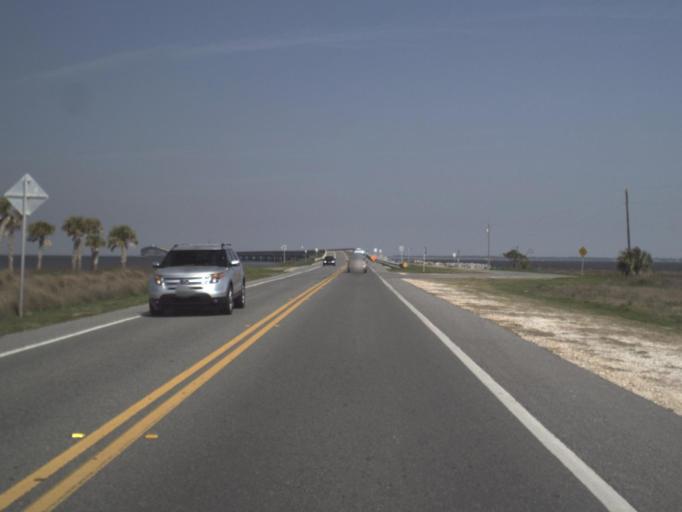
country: US
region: Florida
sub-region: Franklin County
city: Eastpoint
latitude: 29.6674
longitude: -84.8653
